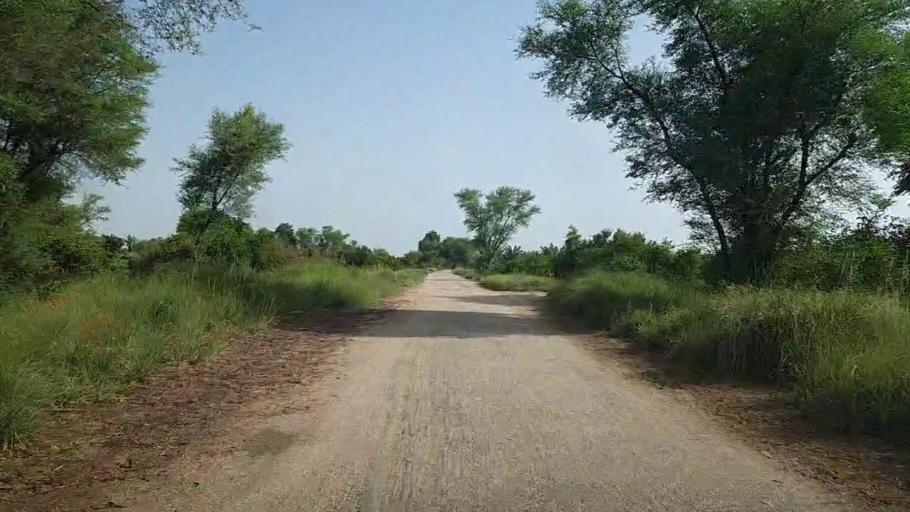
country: PK
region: Sindh
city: Karaundi
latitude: 26.8578
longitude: 68.3309
